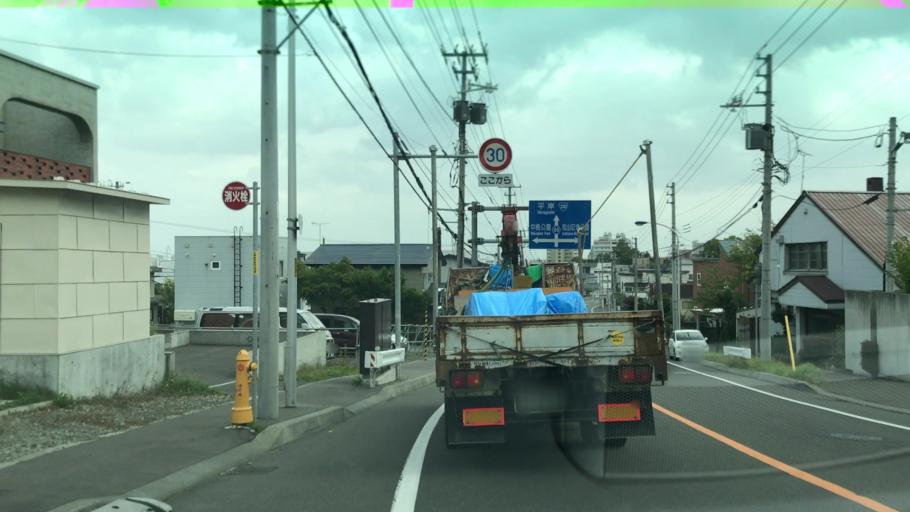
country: JP
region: Hokkaido
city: Sapporo
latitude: 43.0430
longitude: 141.3169
